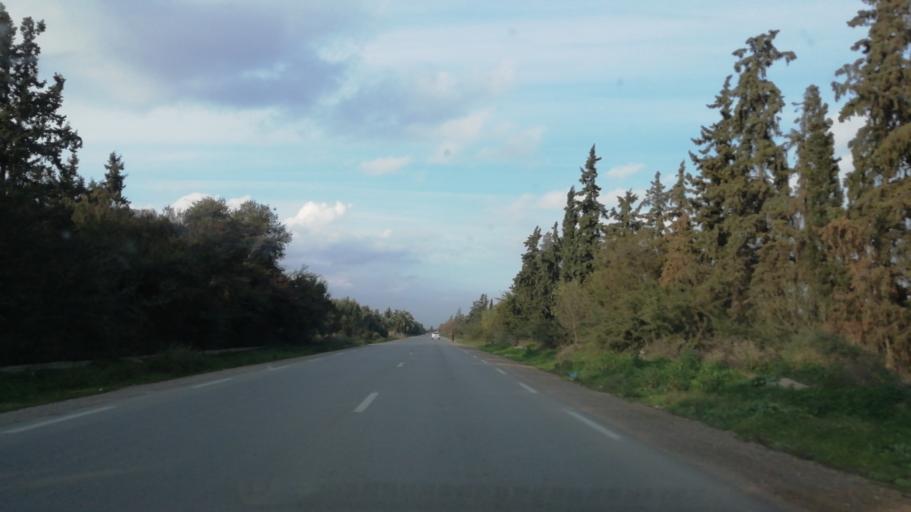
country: DZ
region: Mascara
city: Mascara
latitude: 35.6080
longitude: 0.0522
